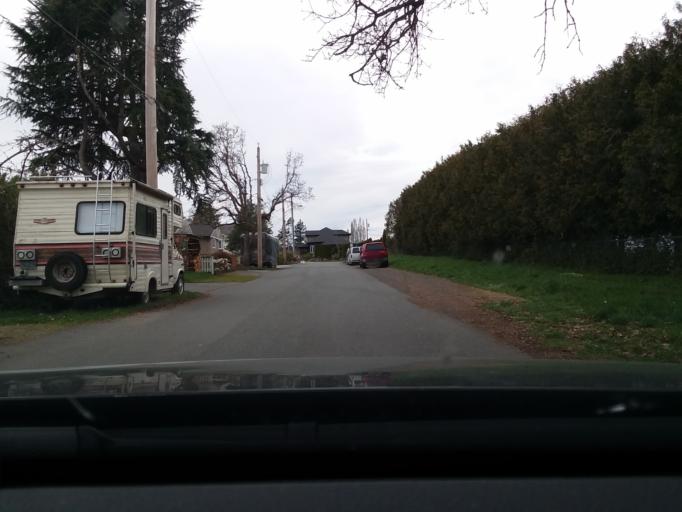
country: CA
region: British Columbia
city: Victoria
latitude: 48.4812
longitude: -123.4101
